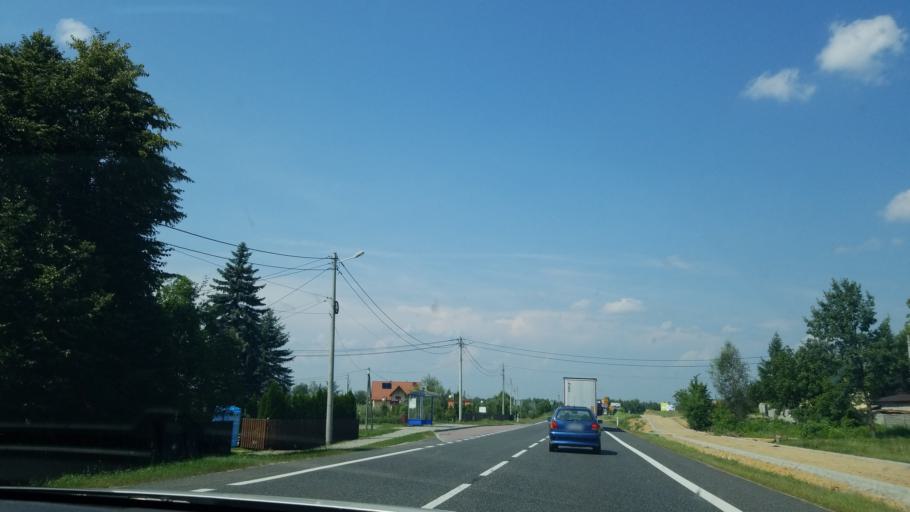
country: PL
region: Subcarpathian Voivodeship
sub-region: Powiat rzeszowski
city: Kamien
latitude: 50.3547
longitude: 22.1238
